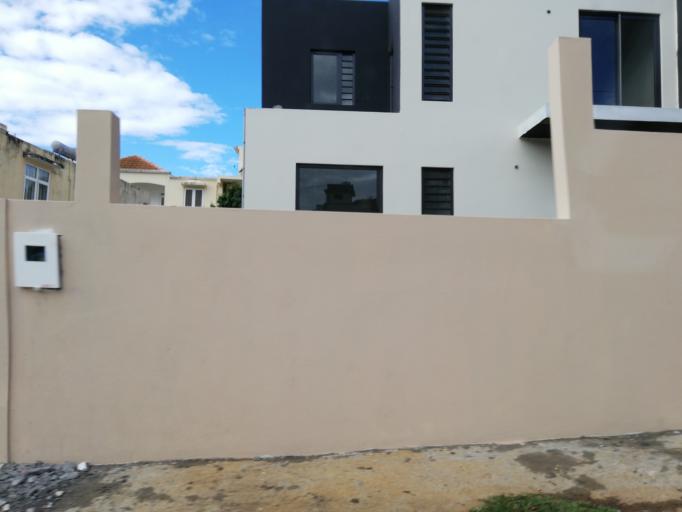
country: MU
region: Black River
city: Petite Riviere
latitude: -20.2037
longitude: 57.4674
